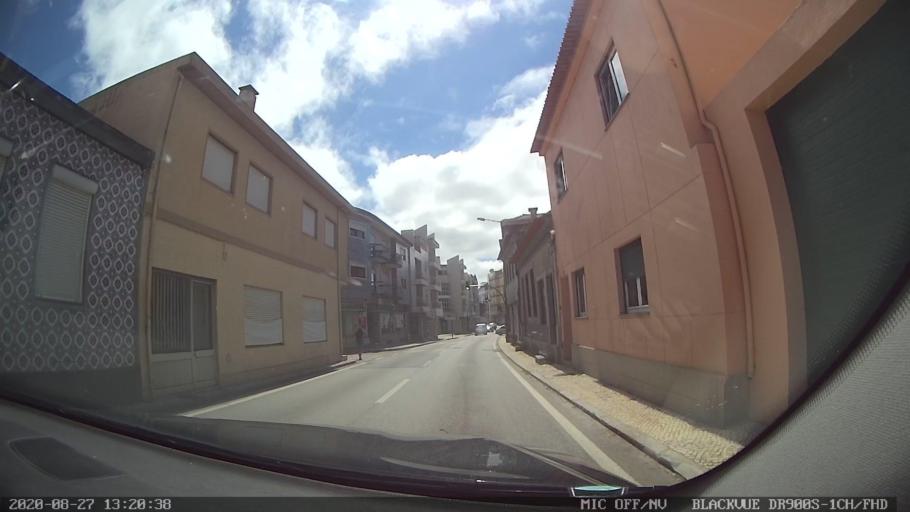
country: PT
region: Aveiro
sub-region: Vagos
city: Vagos
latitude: 40.5558
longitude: -8.6815
